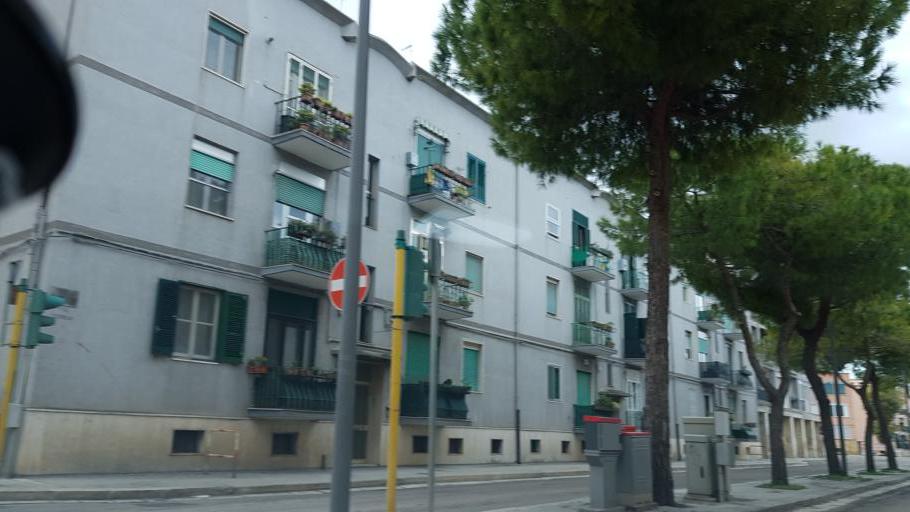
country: IT
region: Apulia
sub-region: Provincia di Brindisi
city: Brindisi
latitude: 40.6298
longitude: 17.9382
